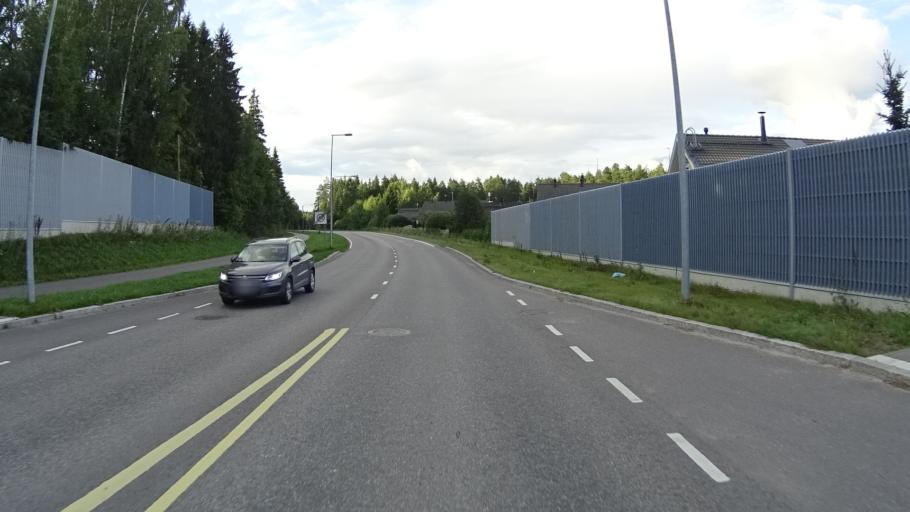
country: FI
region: Uusimaa
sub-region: Helsinki
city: Teekkarikylae
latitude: 60.3191
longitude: 24.8699
